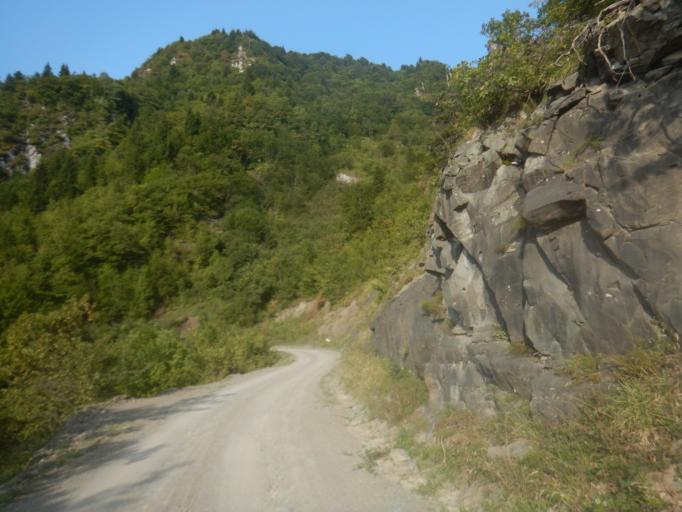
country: TR
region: Ordu
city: Topcam
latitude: 40.7190
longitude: 37.8502
